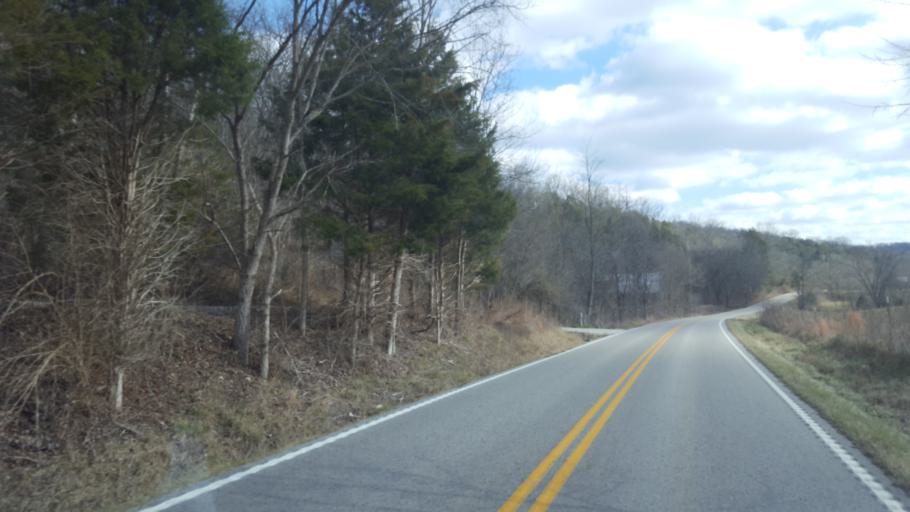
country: US
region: Kentucky
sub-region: Owen County
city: Owenton
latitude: 38.4456
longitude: -84.9011
